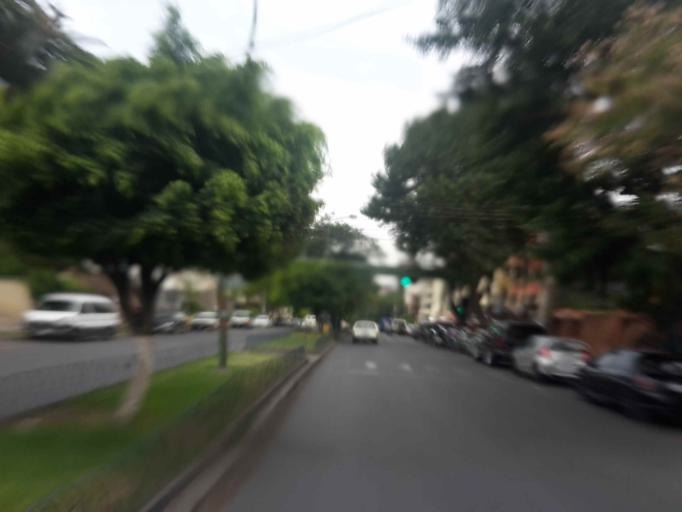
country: BO
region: Cochabamba
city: Cochabamba
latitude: -17.3665
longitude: -66.1665
